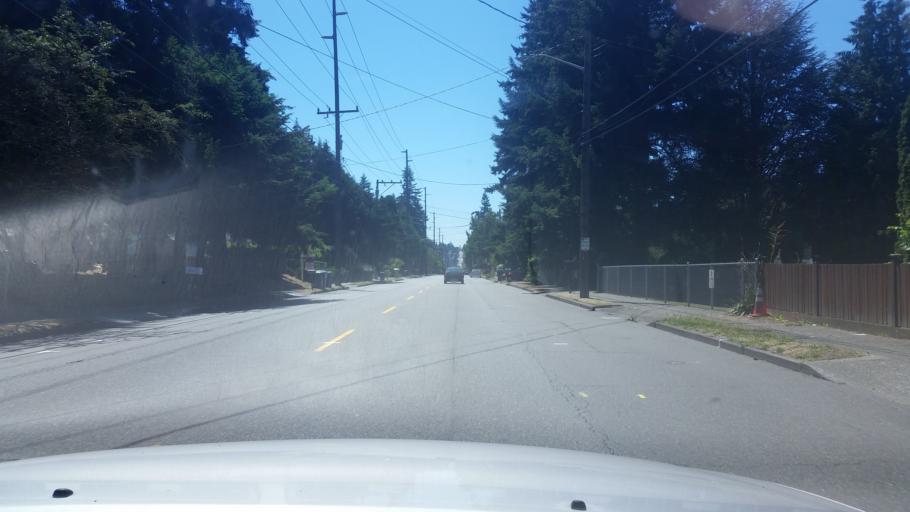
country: US
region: Washington
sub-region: King County
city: Shoreline
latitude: 47.7174
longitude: -122.3236
